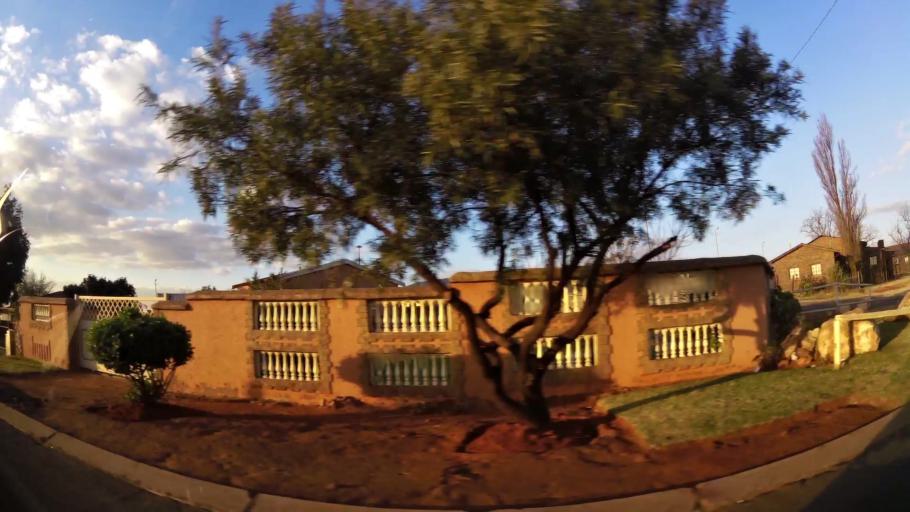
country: ZA
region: Gauteng
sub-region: West Rand District Municipality
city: Krugersdorp
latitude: -26.0731
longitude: 27.7548
